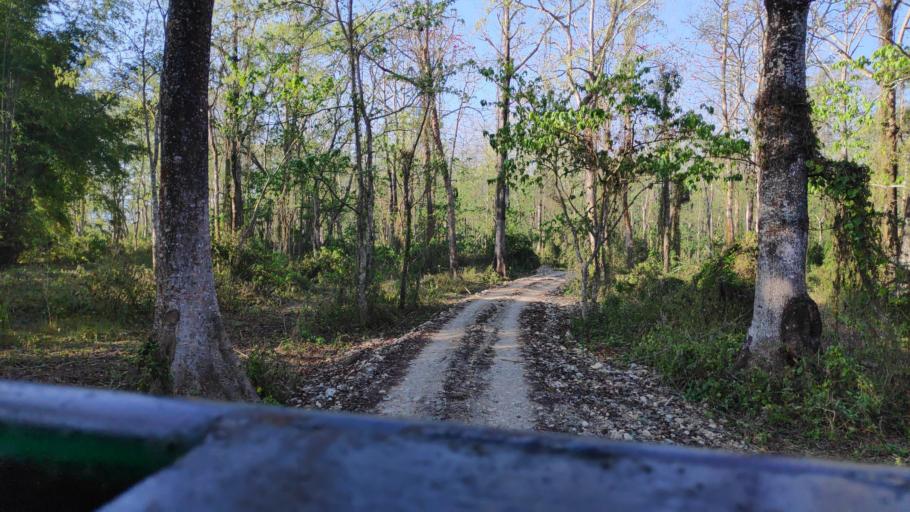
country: NP
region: Central Region
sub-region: Narayani Zone
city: Bharatpur
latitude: 27.5609
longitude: 84.5676
